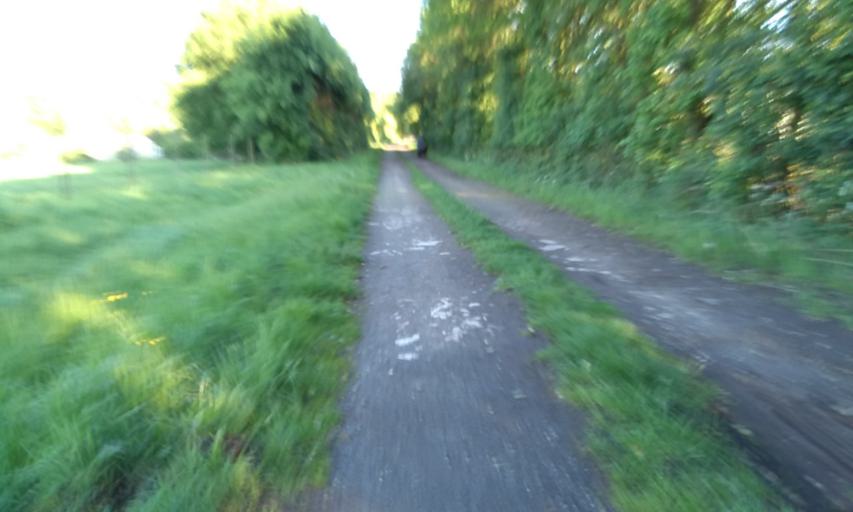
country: DE
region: Lower Saxony
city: Bliedersdorf
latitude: 53.4897
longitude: 9.5692
